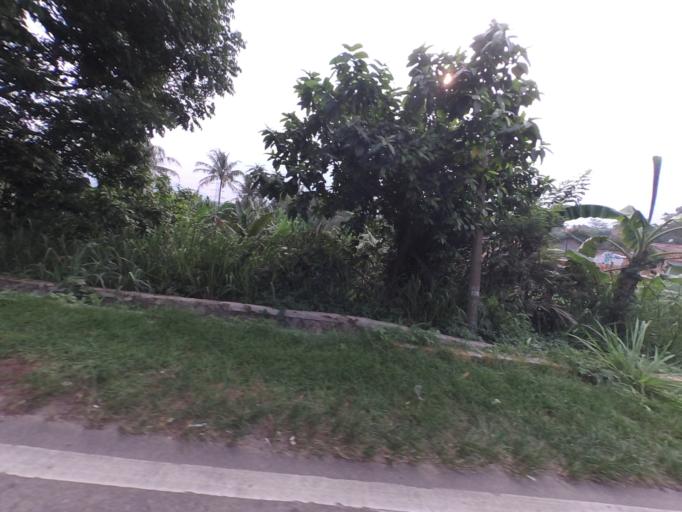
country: ID
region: West Java
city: Sidoger Lebak
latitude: -6.5596
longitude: 106.5748
